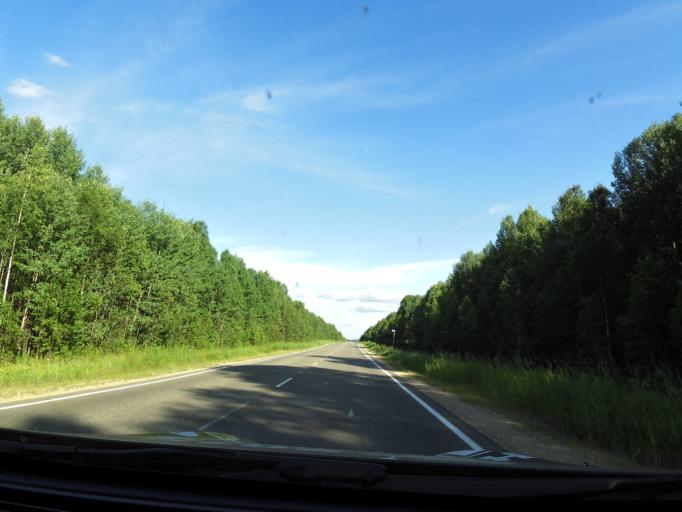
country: RU
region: Kirov
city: Chernaya Kholunitsa
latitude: 58.8168
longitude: 51.8196
